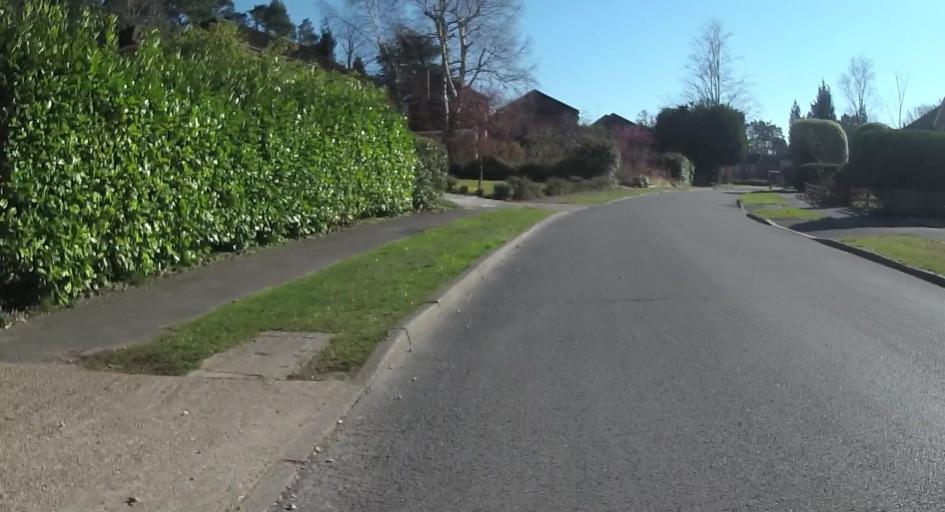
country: GB
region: England
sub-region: Royal Borough of Windsor and Maidenhead
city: Ascot
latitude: 51.4005
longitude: -0.6647
